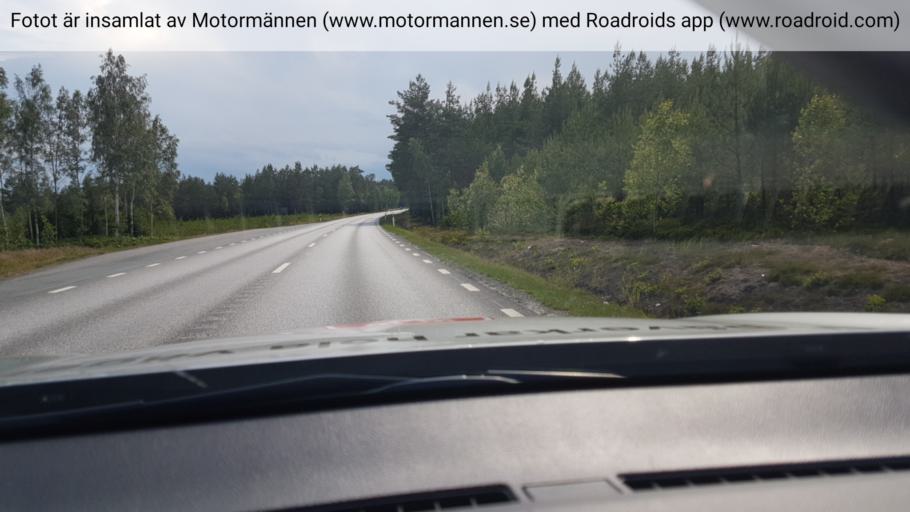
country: SE
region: Joenkoeping
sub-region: Habo Kommun
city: Habo
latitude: 58.0369
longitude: 14.1778
